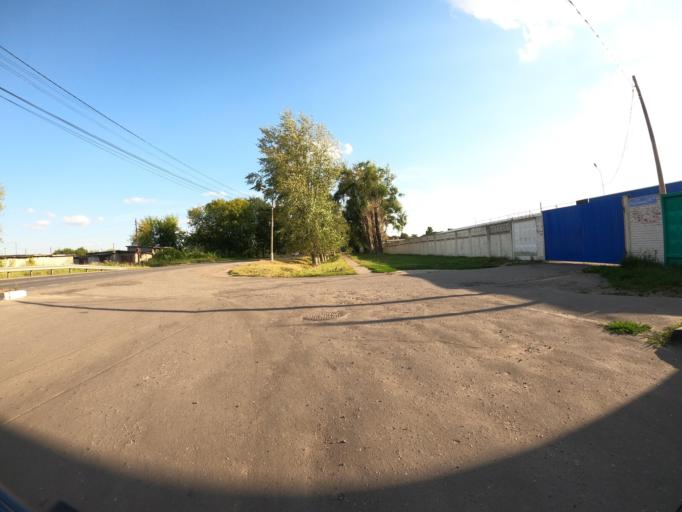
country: RU
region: Moskovskaya
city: Raduzhnyy
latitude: 55.1404
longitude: 38.7317
